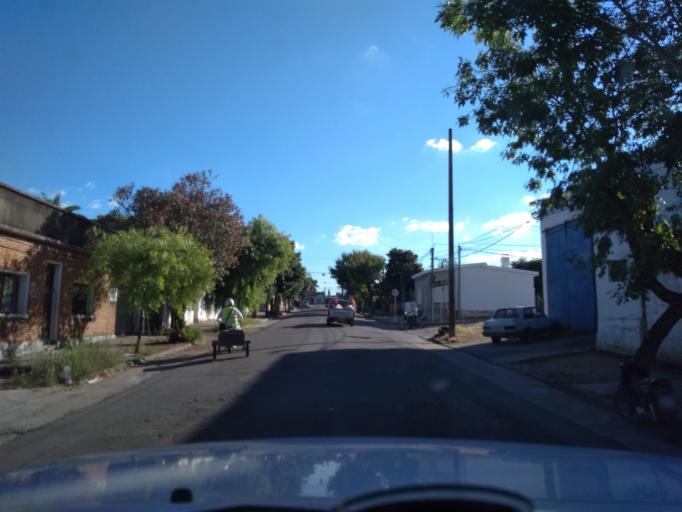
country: UY
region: Florida
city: Florida
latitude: -34.0977
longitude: -56.2255
